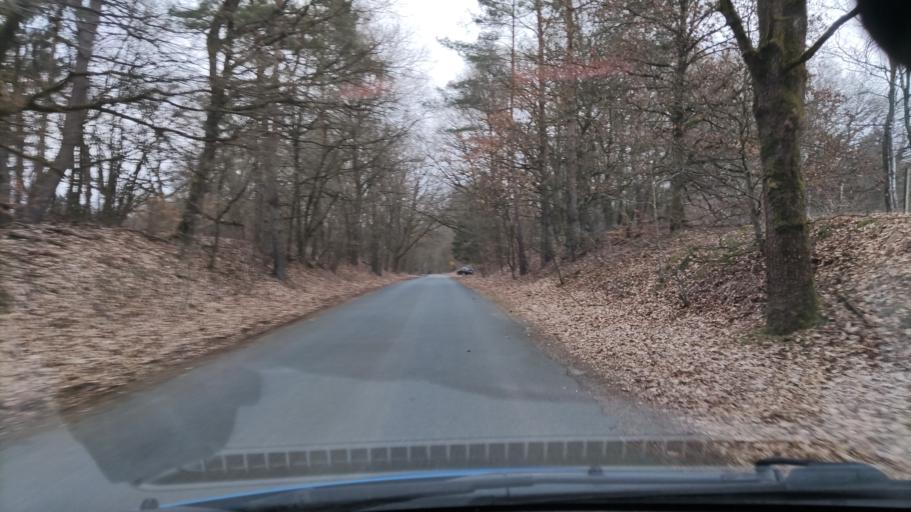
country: DE
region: Lower Saxony
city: Rehlingen
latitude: 53.0590
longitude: 10.2317
